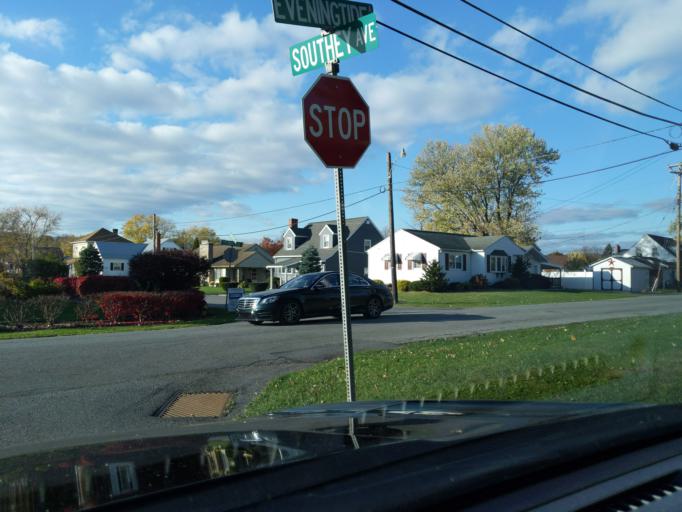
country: US
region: Pennsylvania
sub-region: Blair County
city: Lakemont
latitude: 40.4774
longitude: -78.3994
